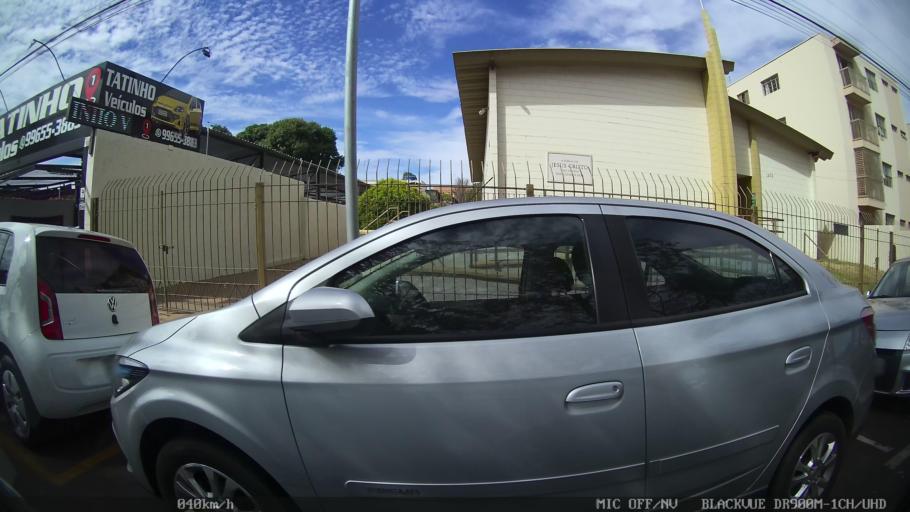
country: BR
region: Sao Paulo
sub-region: Catanduva
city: Catanduva
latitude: -21.1439
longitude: -48.9713
